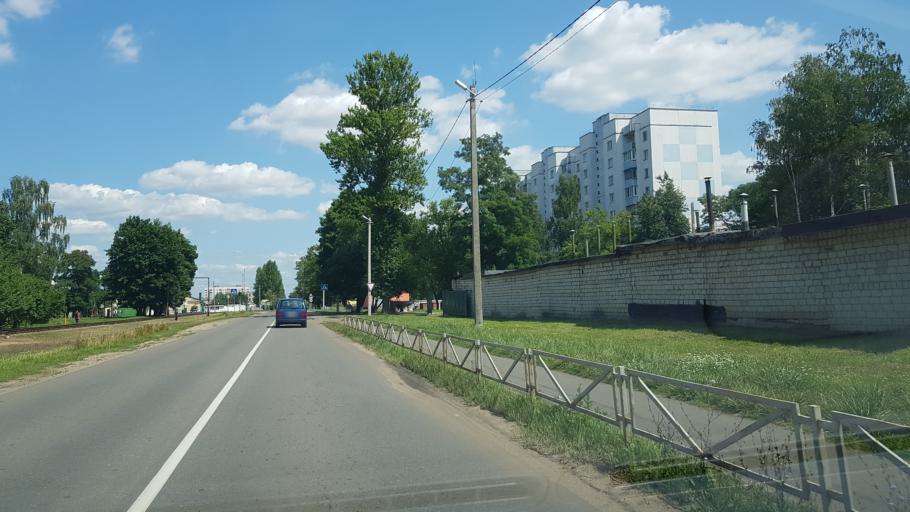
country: BY
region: Mogilev
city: Babruysk
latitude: 53.1174
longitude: 29.2248
